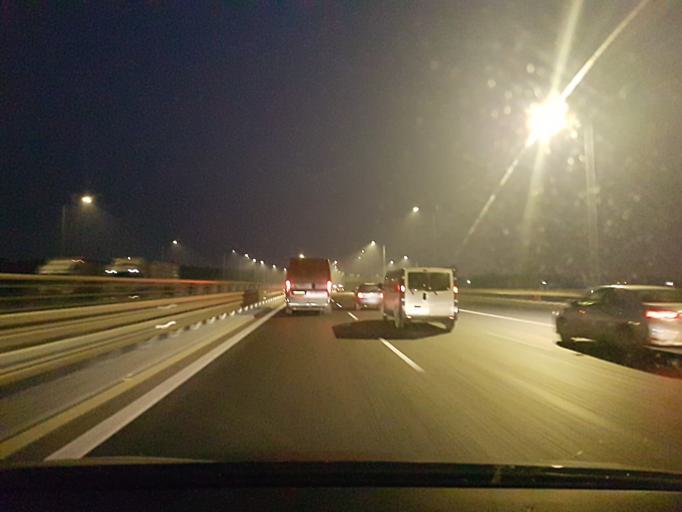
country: PL
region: Masovian Voivodeship
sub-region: Powiat wolominski
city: Marki
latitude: 52.3131
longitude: 21.1265
